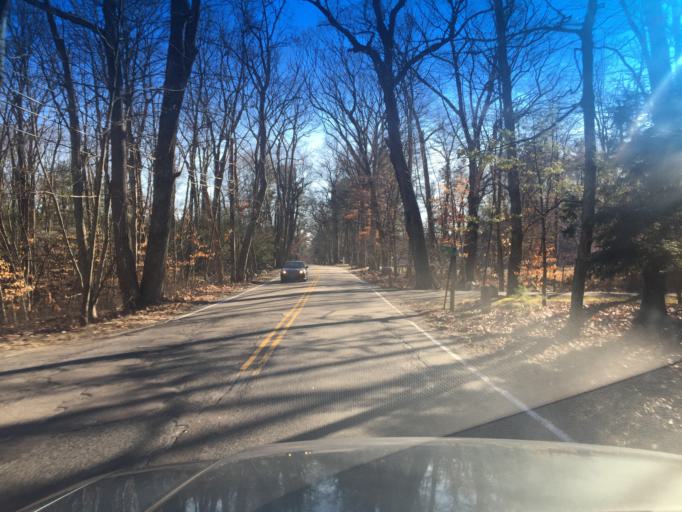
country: US
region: Massachusetts
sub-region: Norfolk County
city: Millis
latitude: 42.1925
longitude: -71.3835
